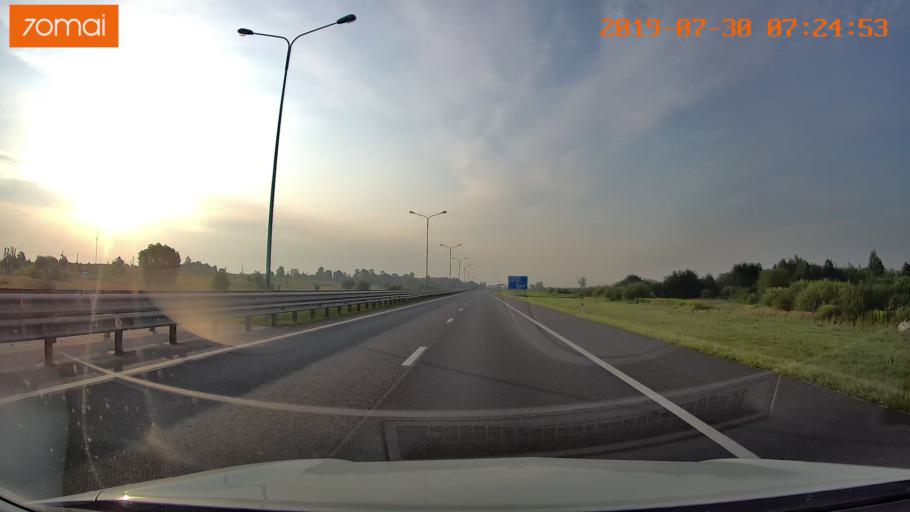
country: RU
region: Kaliningrad
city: Bol'shoe Isakovo
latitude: 54.6904
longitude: 20.8232
